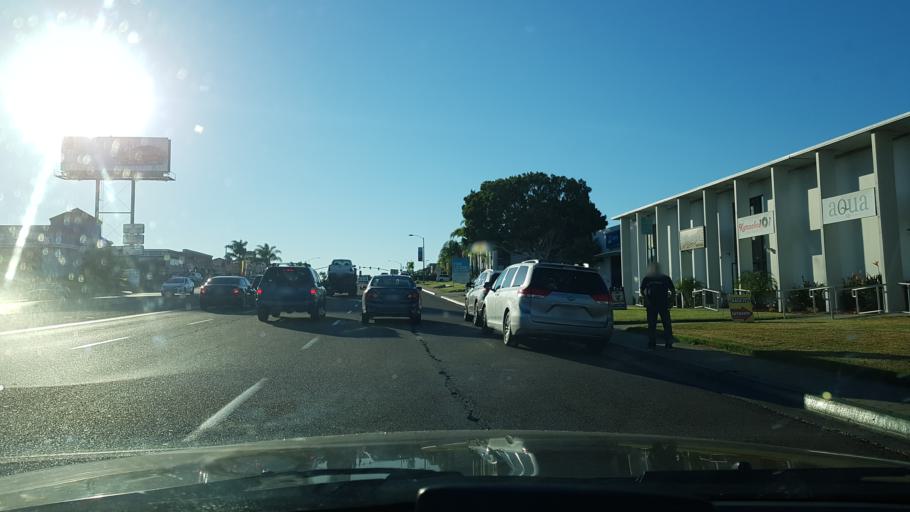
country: US
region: California
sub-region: San Diego County
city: San Diego
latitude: 32.8328
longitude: -117.1560
